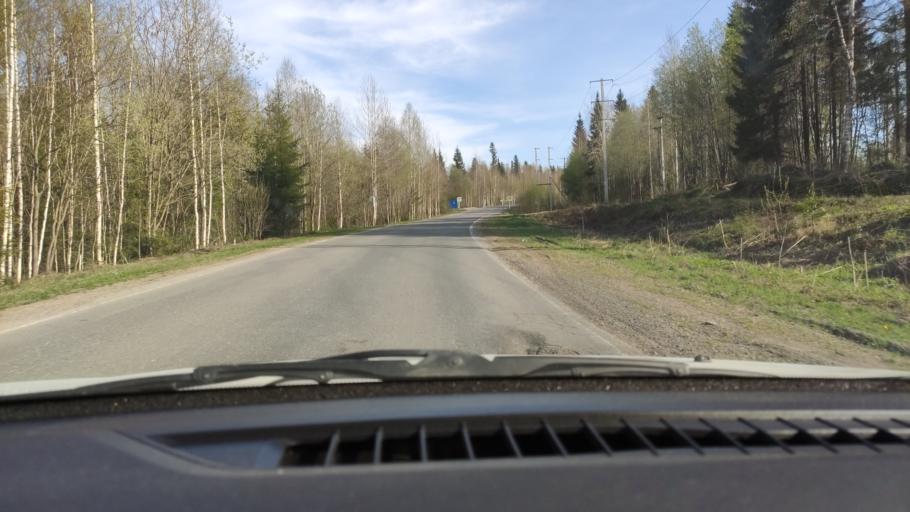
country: RU
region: Perm
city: Novyye Lyady
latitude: 57.9555
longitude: 56.5663
